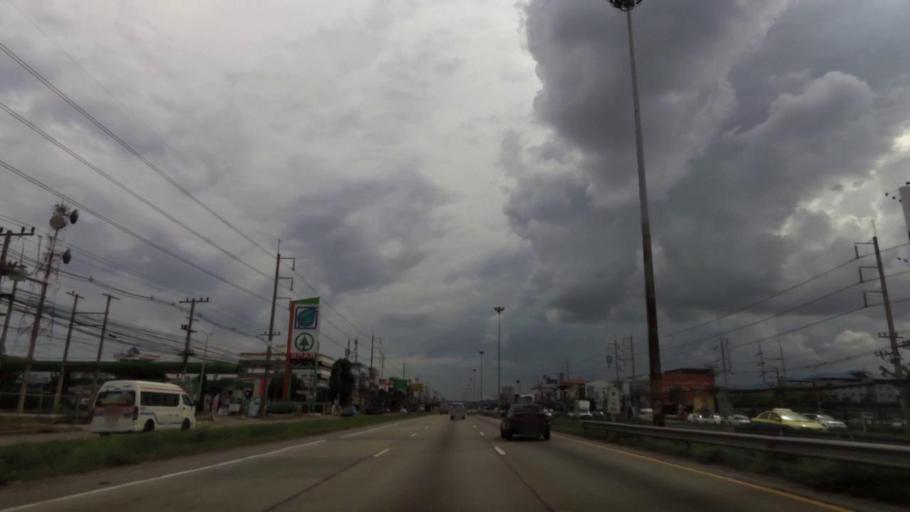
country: TH
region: Phra Nakhon Si Ayutthaya
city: Bang Pa-in
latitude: 14.1507
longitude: 100.6184
